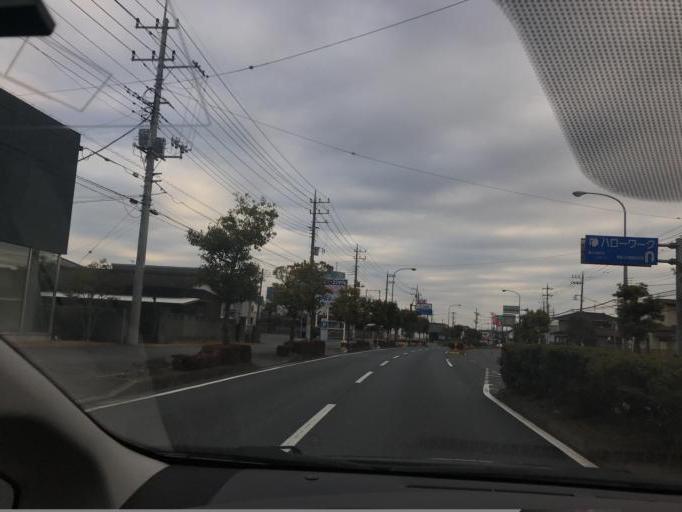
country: JP
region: Ibaraki
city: Mitsukaido
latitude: 36.0144
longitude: 139.9908
